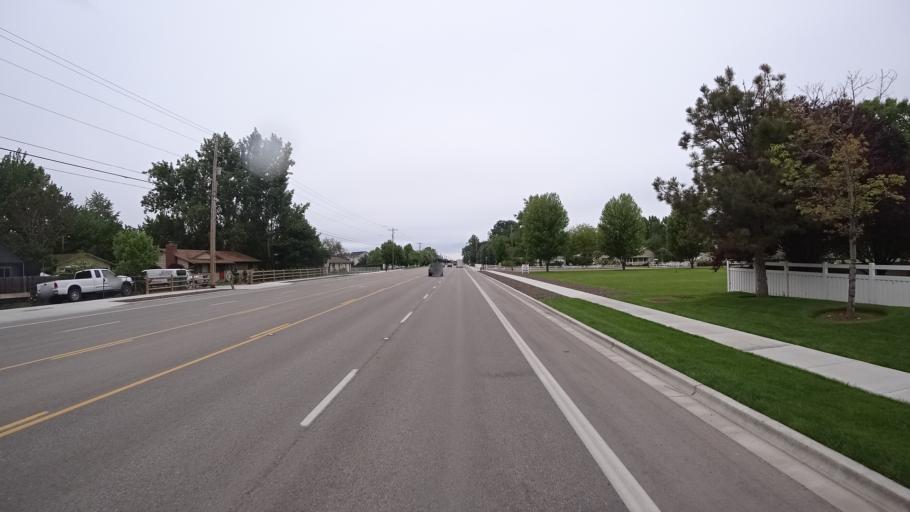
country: US
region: Idaho
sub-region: Ada County
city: Meridian
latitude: 43.6338
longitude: -116.3806
